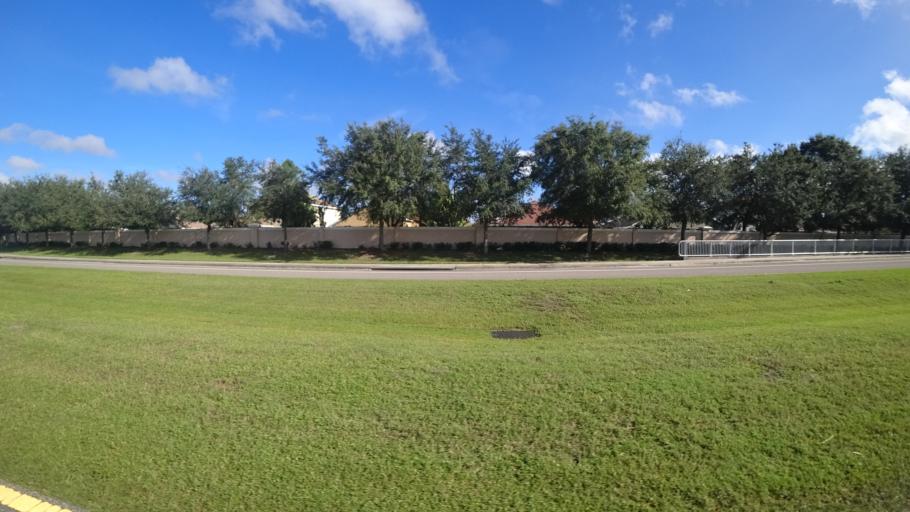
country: US
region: Florida
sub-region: Manatee County
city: Ellenton
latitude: 27.5759
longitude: -82.5126
